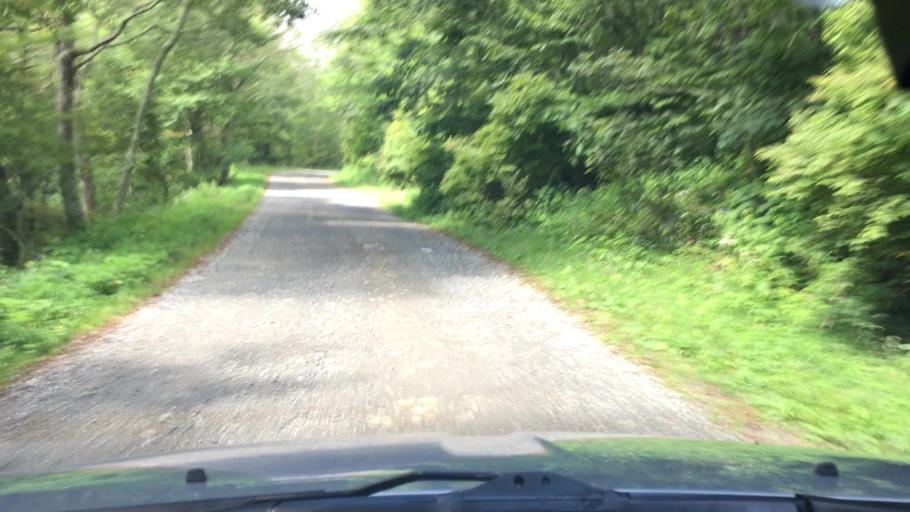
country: US
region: Tennessee
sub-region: Unicoi County
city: Banner Hill
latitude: 35.9868
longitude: -82.4909
